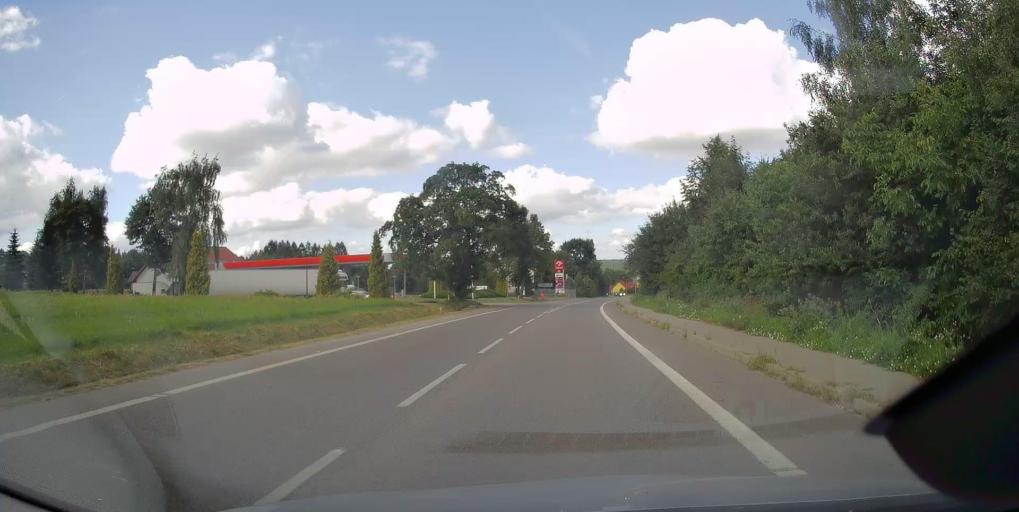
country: PL
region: Swietokrzyskie
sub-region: Powiat kielecki
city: Nowa Slupia
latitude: 50.8539
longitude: 21.0858
